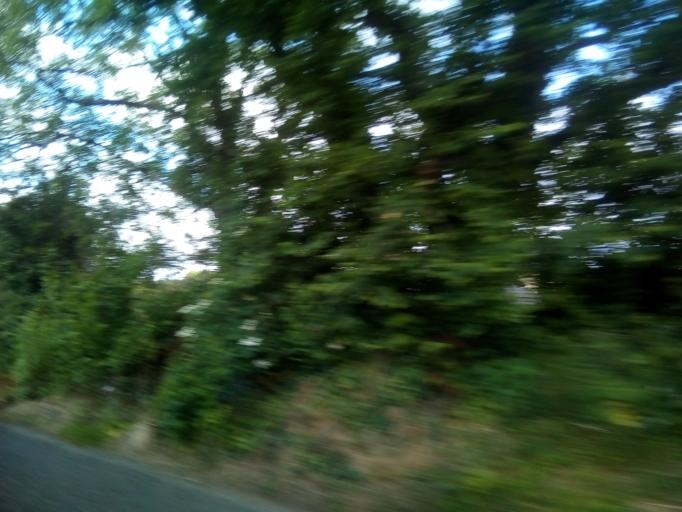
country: IE
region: Leinster
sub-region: Loch Garman
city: Loch Garman
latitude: 52.2822
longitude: -6.5386
